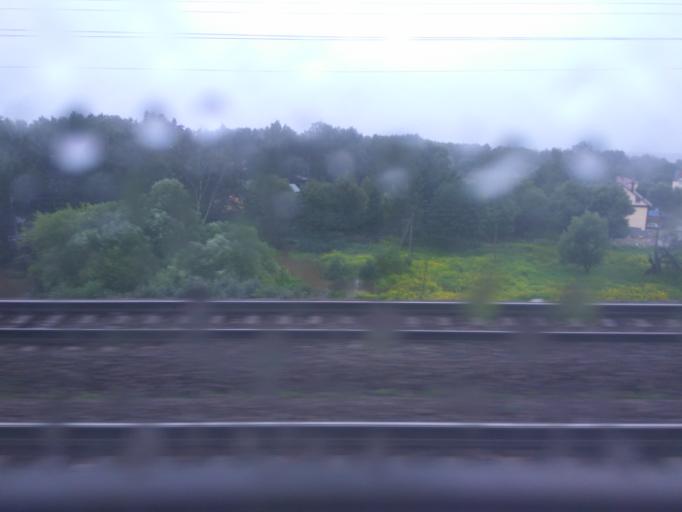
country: RU
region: Moscow
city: Zagor'ye
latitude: 55.5532
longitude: 37.6793
